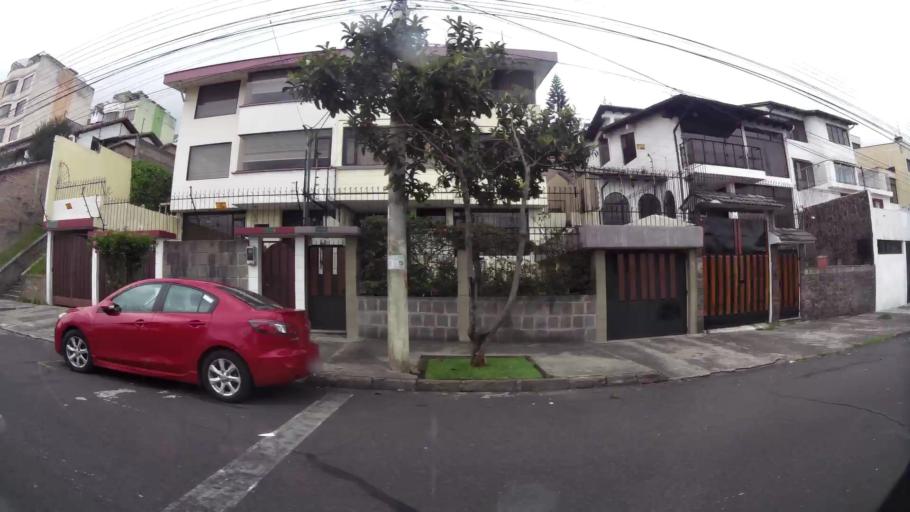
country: EC
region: Pichincha
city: Quito
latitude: -0.2036
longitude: -78.5094
